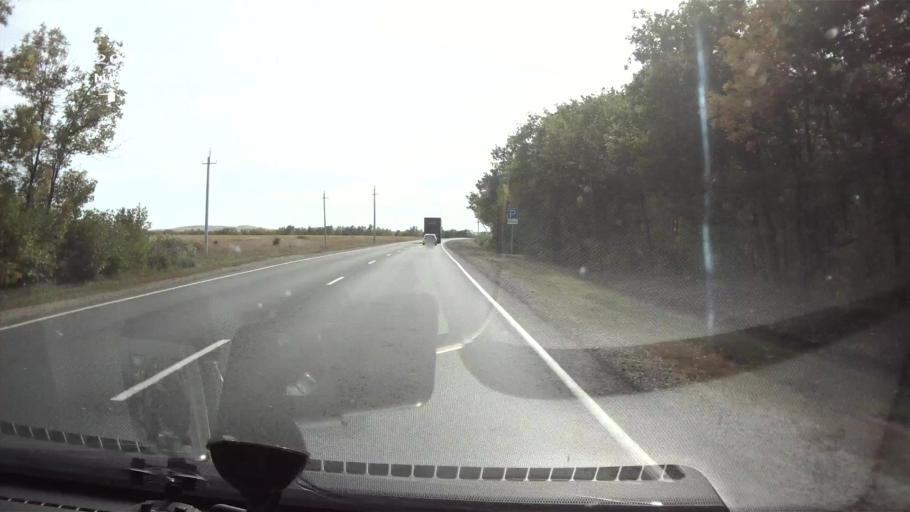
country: RU
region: Saratov
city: Alekseyevka
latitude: 52.2728
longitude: 47.9298
